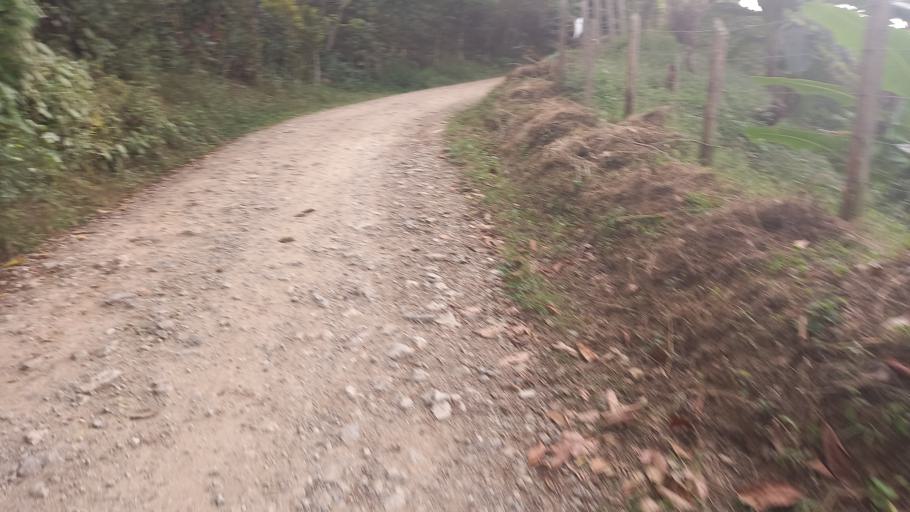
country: CO
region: Antioquia
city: Santa Barbara
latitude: 5.8338
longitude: -75.5765
